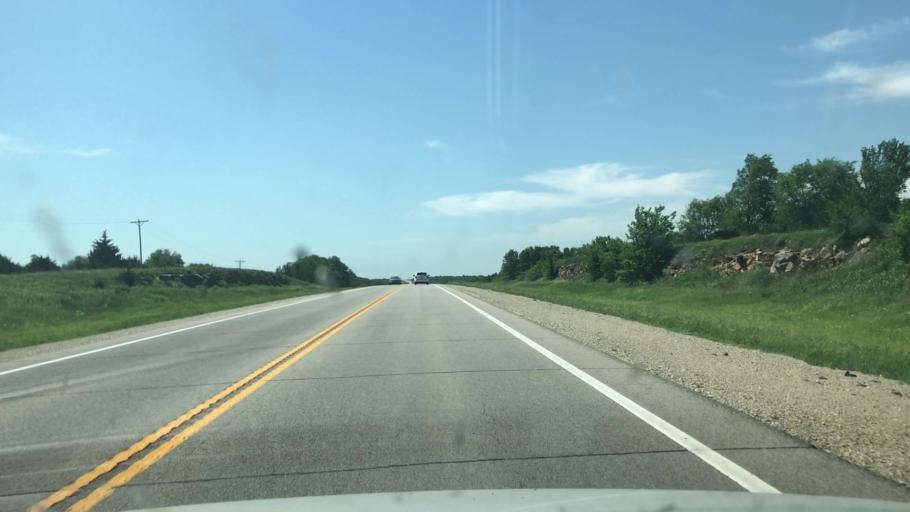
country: US
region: Kansas
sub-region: Cowley County
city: Winfield
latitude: 37.3705
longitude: -97.0071
